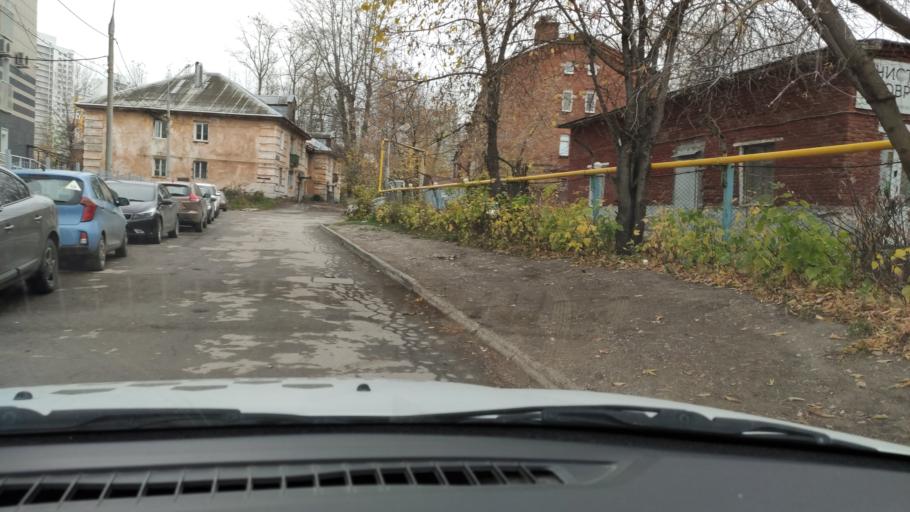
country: RU
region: Perm
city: Perm
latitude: 57.9946
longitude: 56.2713
